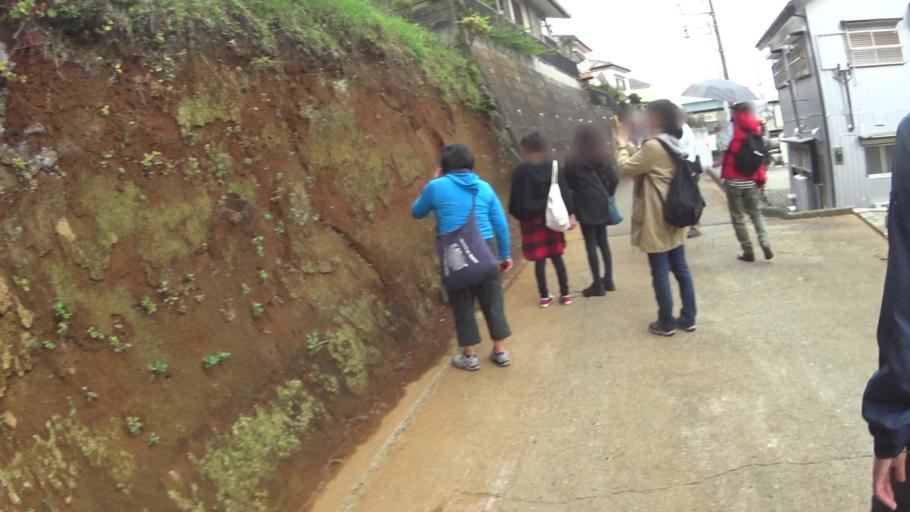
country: JP
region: Kanagawa
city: Hadano
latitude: 35.3914
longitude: 139.2208
